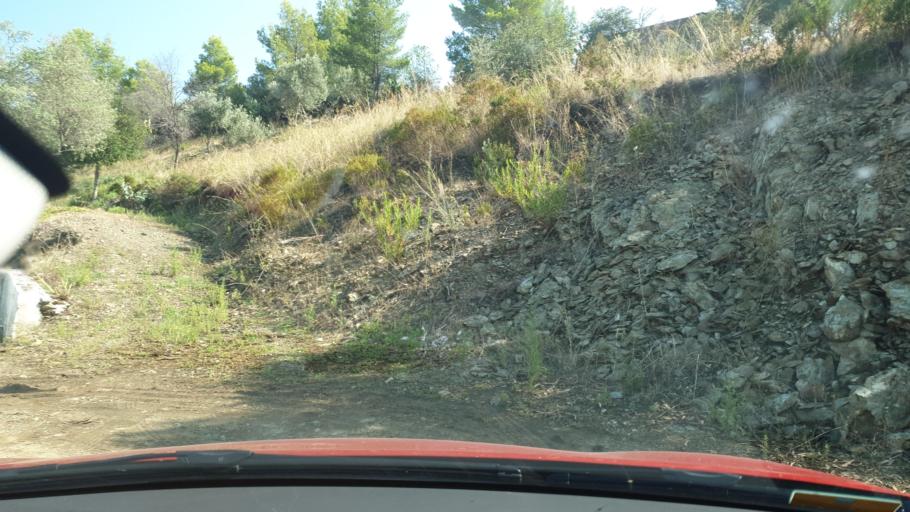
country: GR
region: Central Macedonia
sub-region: Nomos Chalkidikis
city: Sykia
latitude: 39.9785
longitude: 23.9085
